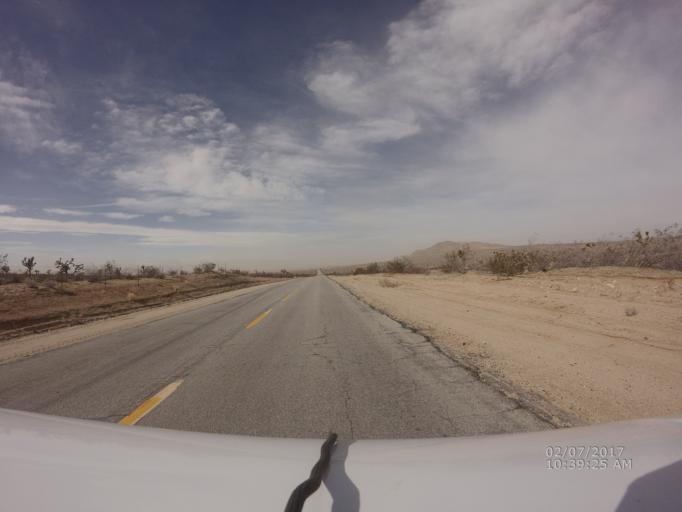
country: US
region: California
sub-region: Los Angeles County
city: Lake Los Angeles
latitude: 34.6902
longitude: -117.7975
